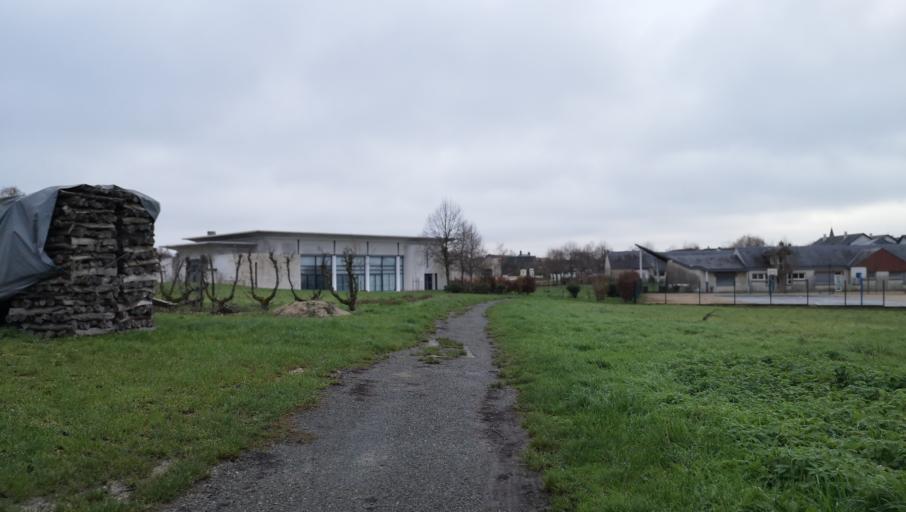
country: FR
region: Centre
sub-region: Departement du Loiret
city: Semoy
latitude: 47.9338
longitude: 1.9448
